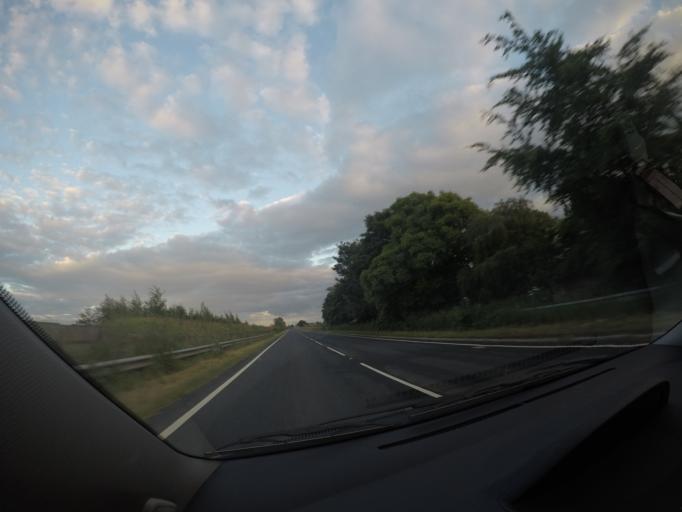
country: GB
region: England
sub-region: North Yorkshire
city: Bedale
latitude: 54.2540
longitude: -1.5110
